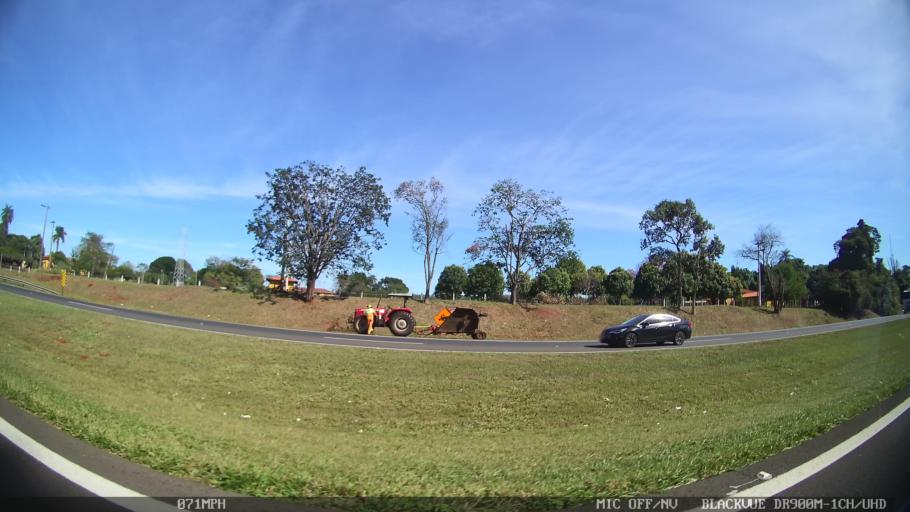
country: BR
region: Sao Paulo
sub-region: Pirassununga
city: Pirassununga
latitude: -21.9633
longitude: -47.4575
